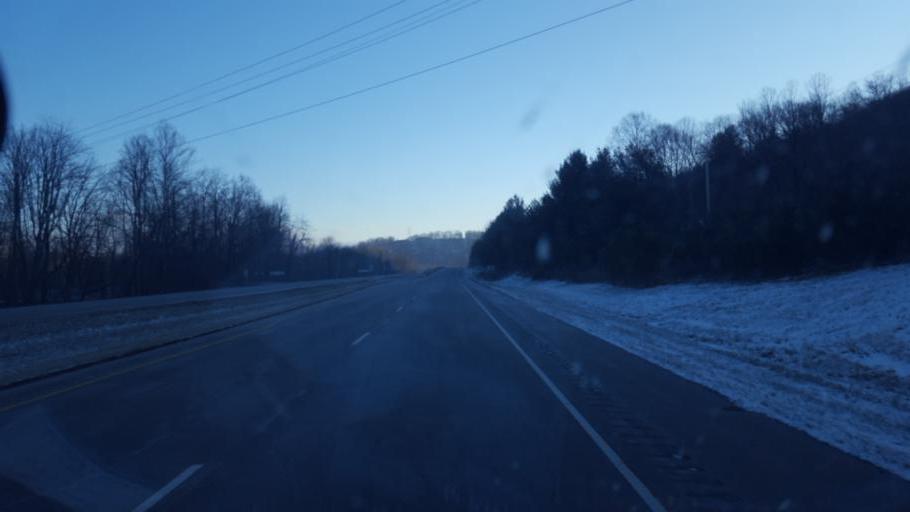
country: US
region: Ohio
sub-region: Pike County
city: Piketon
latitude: 39.0461
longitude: -83.1403
